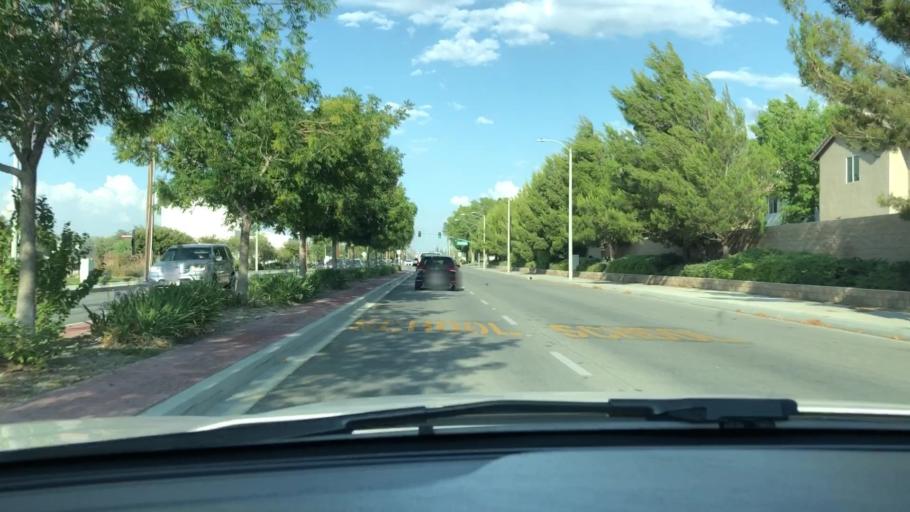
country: US
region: California
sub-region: Los Angeles County
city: Quartz Hill
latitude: 34.6748
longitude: -118.1901
